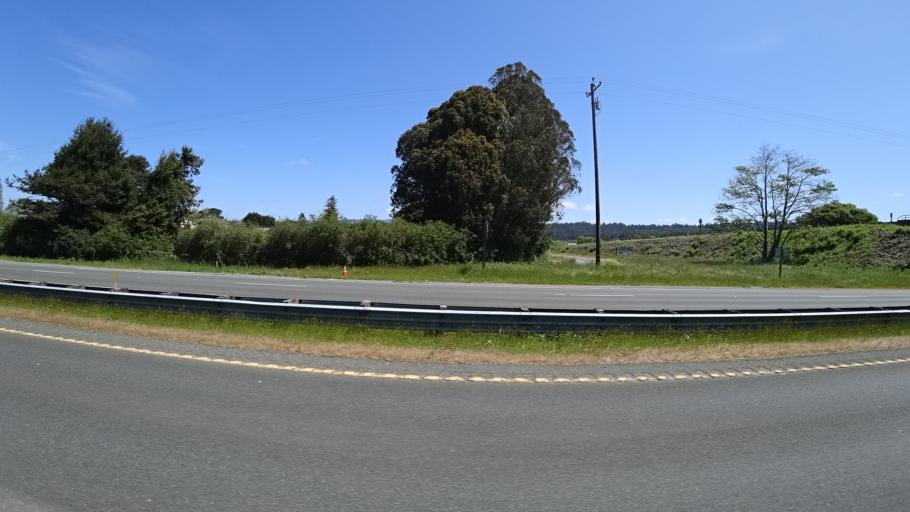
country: US
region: California
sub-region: Humboldt County
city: Arcata
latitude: 40.8979
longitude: -124.0837
